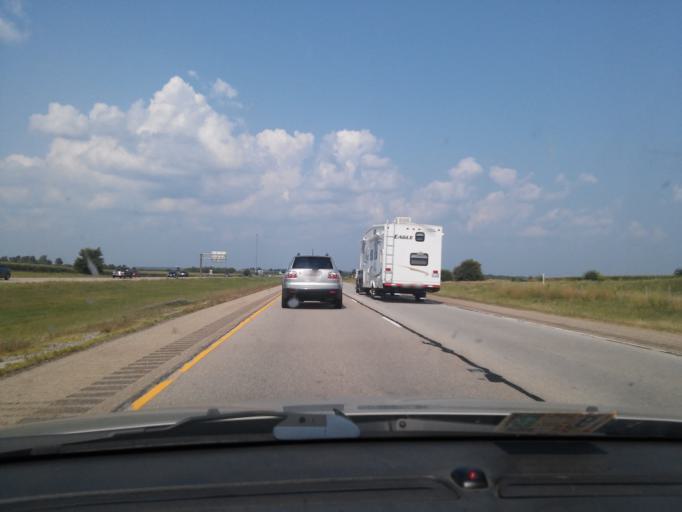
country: US
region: Illinois
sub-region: McLean County
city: Normal
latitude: 40.5430
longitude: -88.9318
